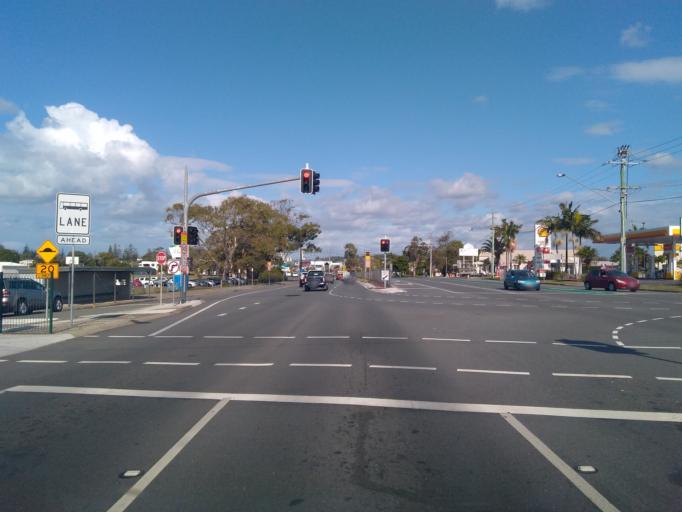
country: AU
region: Queensland
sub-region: Gold Coast
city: Varsity Lakes
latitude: -28.0633
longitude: 153.4378
